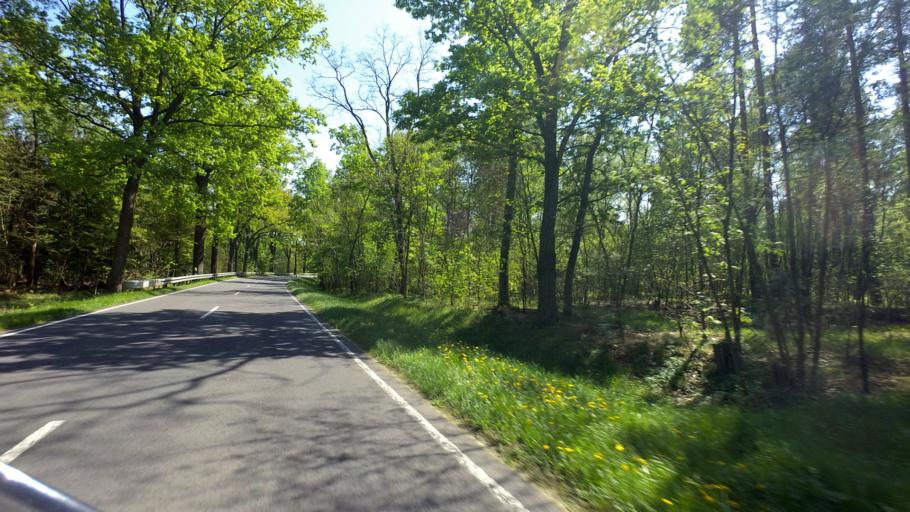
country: DE
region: Brandenburg
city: Schlepzig
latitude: 52.0660
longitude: 13.9144
